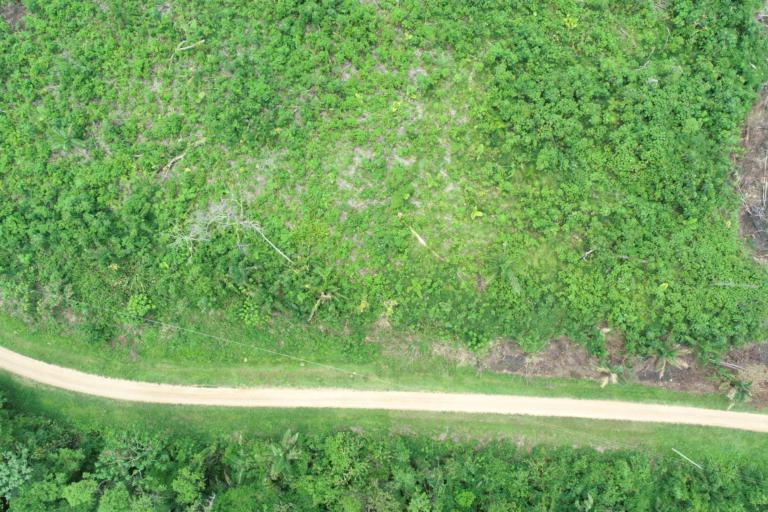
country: BO
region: El Beni
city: San Borja
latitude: -14.7410
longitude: -67.1663
